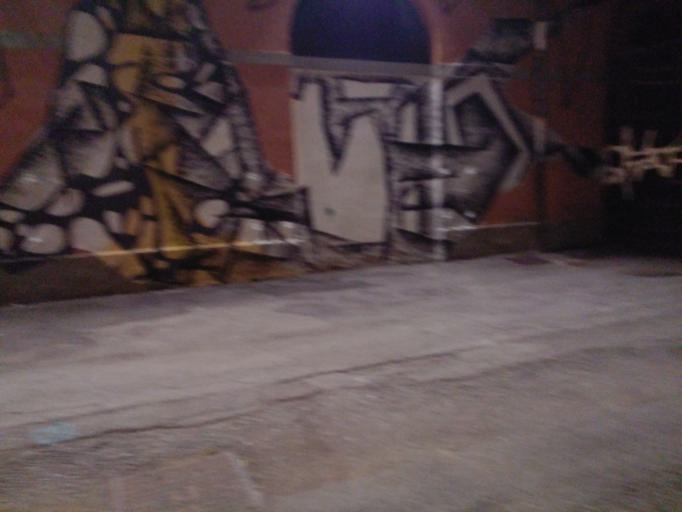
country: IT
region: Tuscany
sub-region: Provincia di Prato
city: Prato
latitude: 43.8770
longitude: 11.0903
